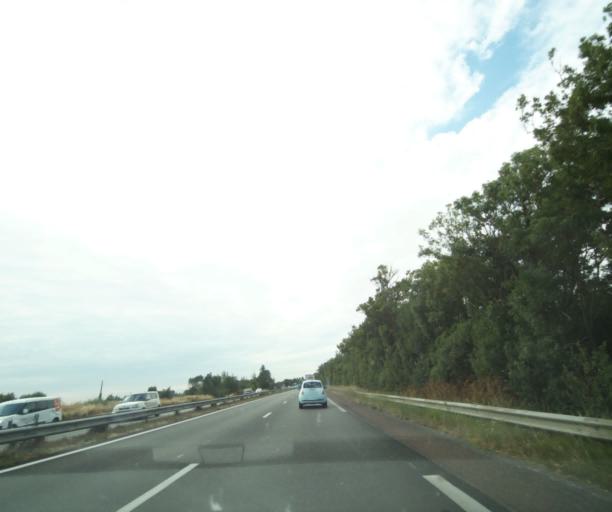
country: FR
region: Poitou-Charentes
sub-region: Departement de la Charente-Maritime
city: Angoulins
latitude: 46.1151
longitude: -1.1046
